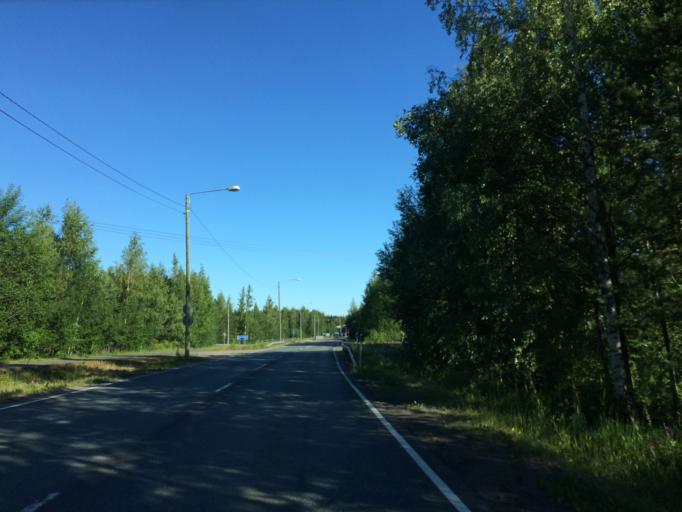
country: FI
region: Haeme
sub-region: Haemeenlinna
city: Haemeenlinna
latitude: 60.9625
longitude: 24.4518
